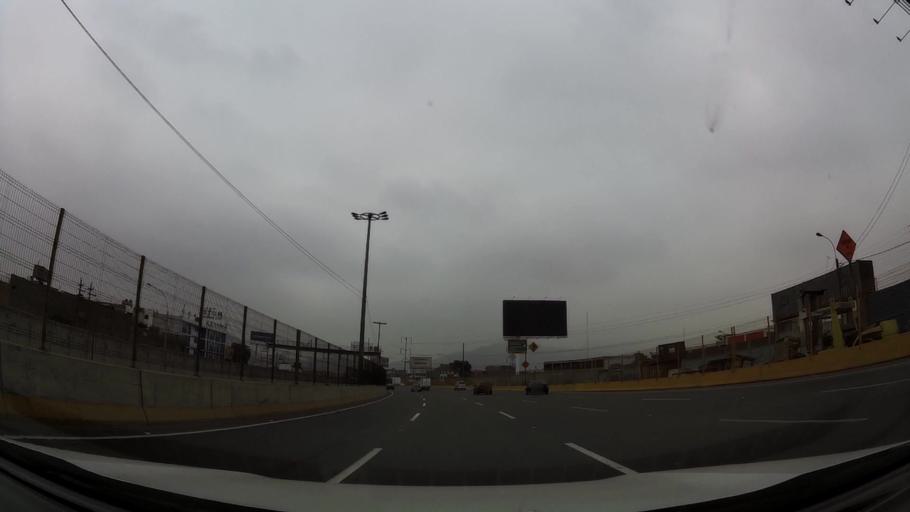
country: PE
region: Lima
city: Lima
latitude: -12.0292
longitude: -76.9957
